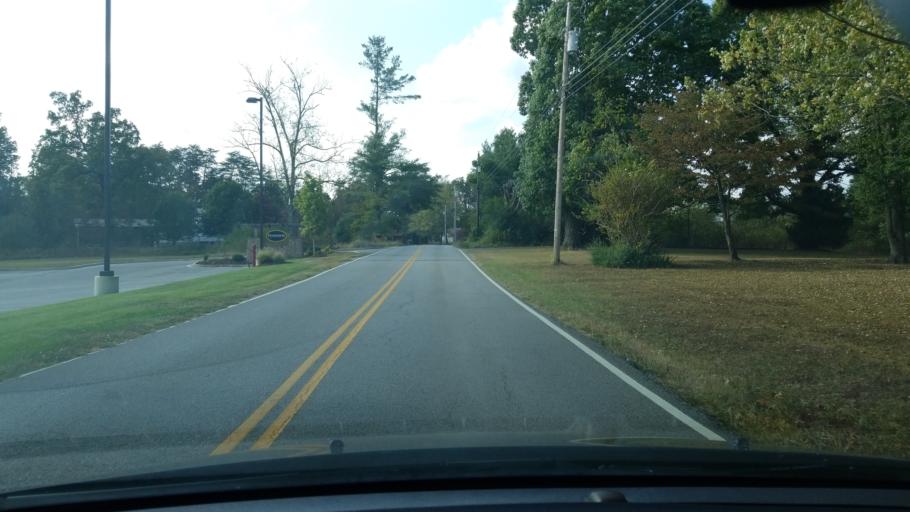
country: US
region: Tennessee
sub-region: Cumberland County
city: Crossville
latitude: 35.9807
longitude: -85.0291
